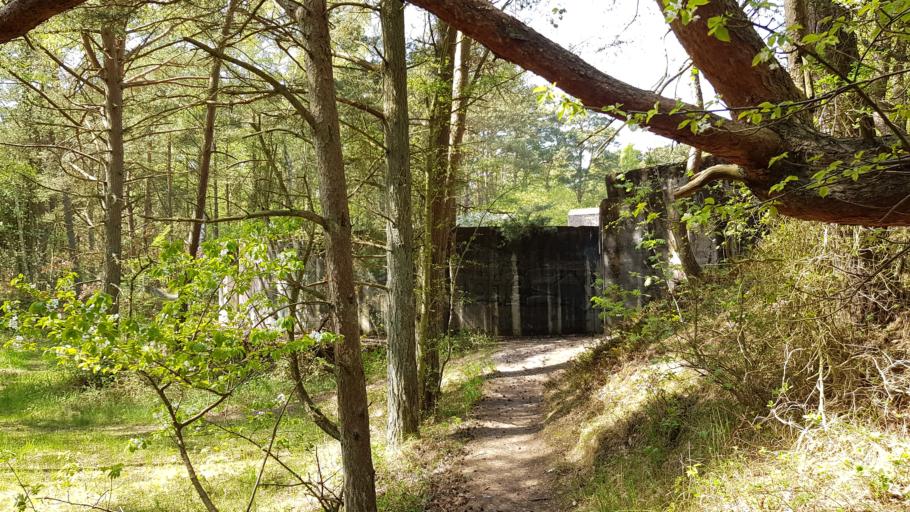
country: DK
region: Capital Region
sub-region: Bornholm Kommune
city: Nexo
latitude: 55.0008
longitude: 15.0813
